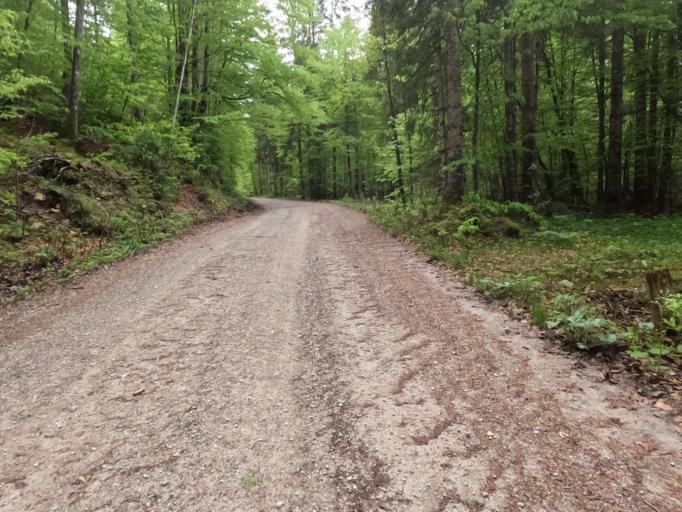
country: DE
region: Bavaria
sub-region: Upper Bavaria
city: Ruhpolding
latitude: 47.7134
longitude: 12.6590
